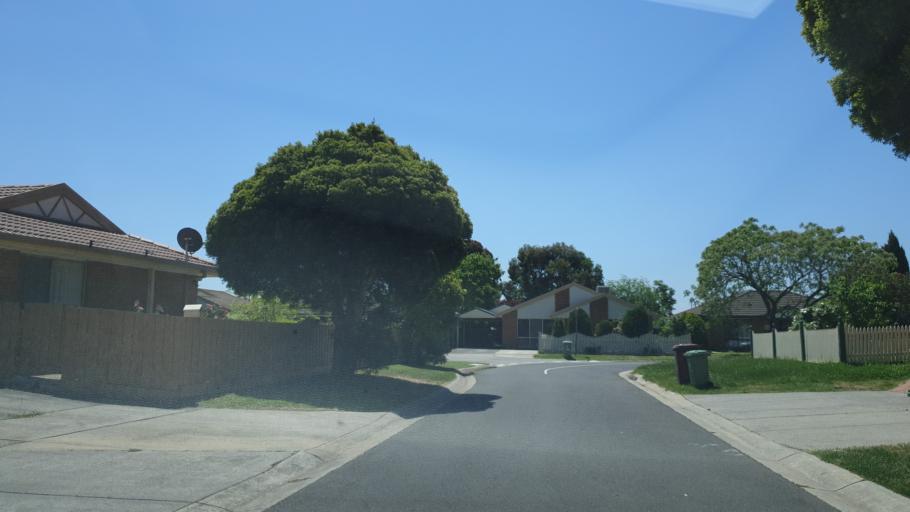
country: AU
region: Victoria
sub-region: Casey
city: Narre Warren South
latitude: -38.0585
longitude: 145.2914
